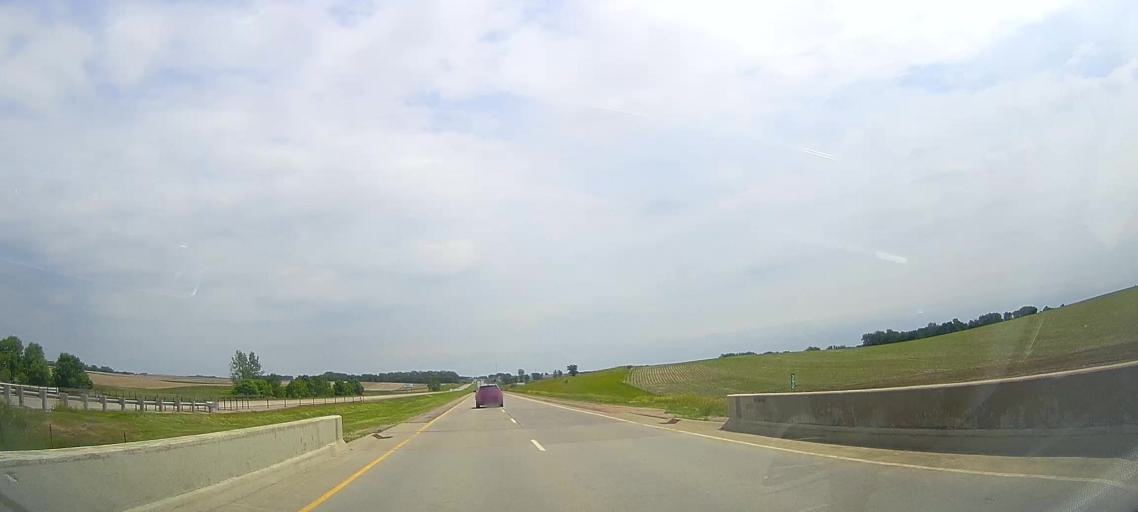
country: US
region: South Dakota
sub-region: Minnehaha County
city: Crooks
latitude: 43.6085
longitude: -96.8500
